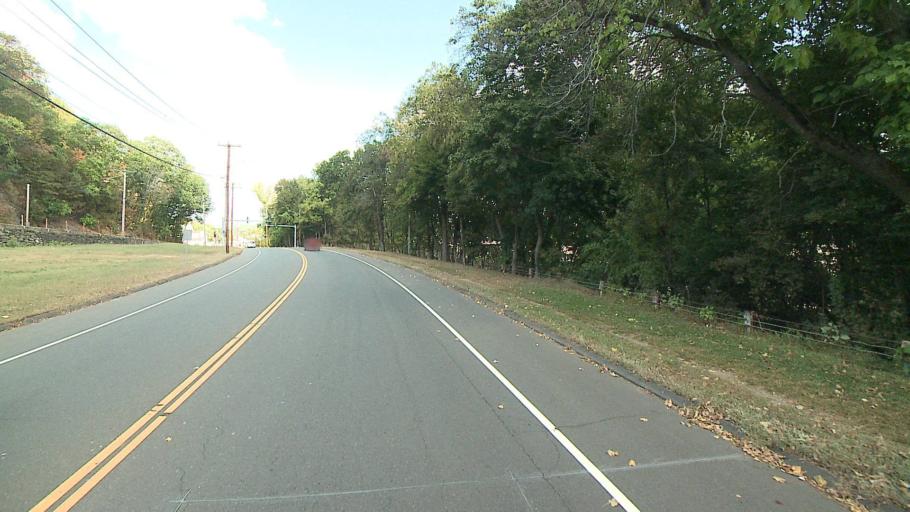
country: US
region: Connecticut
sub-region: New Haven County
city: Ansonia
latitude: 41.3379
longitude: -73.0823
